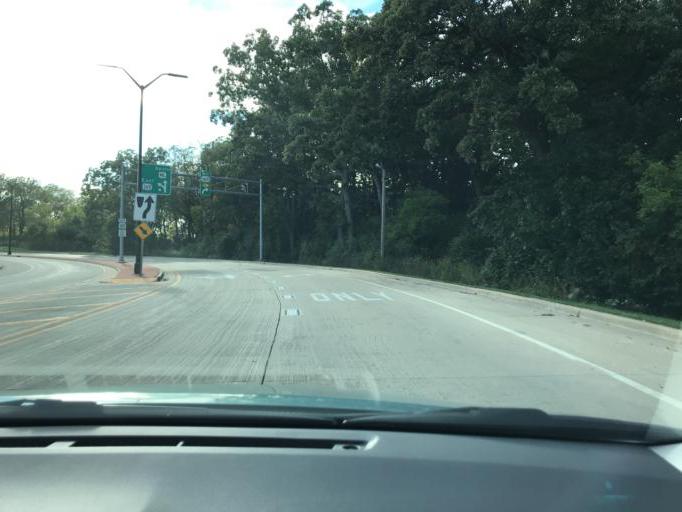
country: US
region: Illinois
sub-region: Lake County
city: Winthrop Harbor
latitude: 42.5237
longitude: -87.8591
